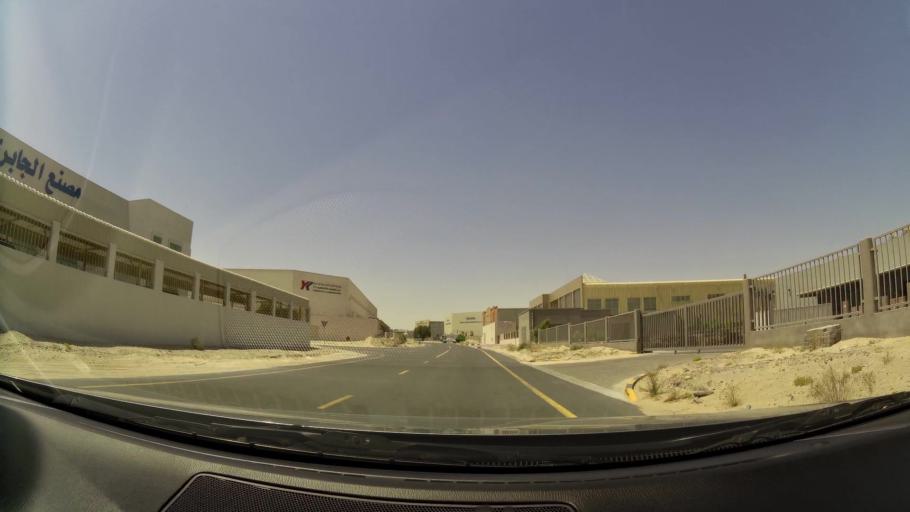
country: AE
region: Dubai
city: Dubai
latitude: 24.9767
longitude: 55.1898
